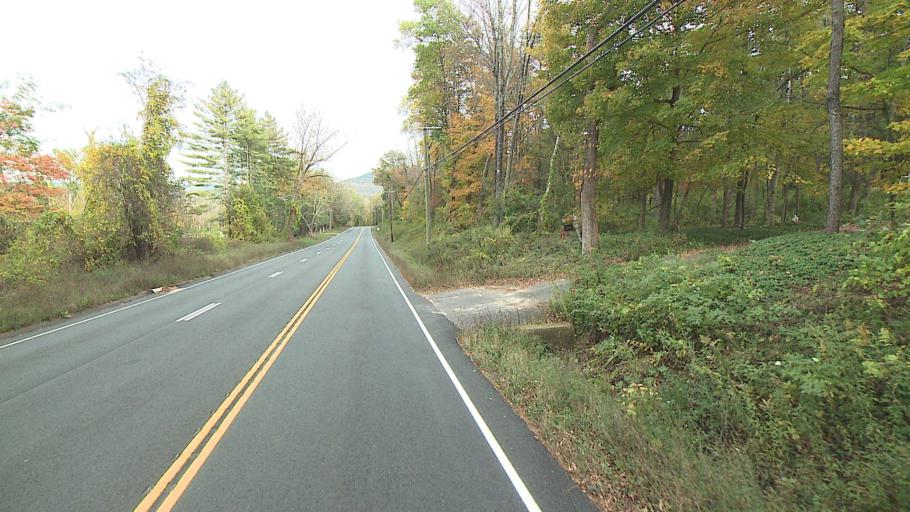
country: US
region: Connecticut
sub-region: Litchfield County
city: Canaan
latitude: 42.0030
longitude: -73.3794
